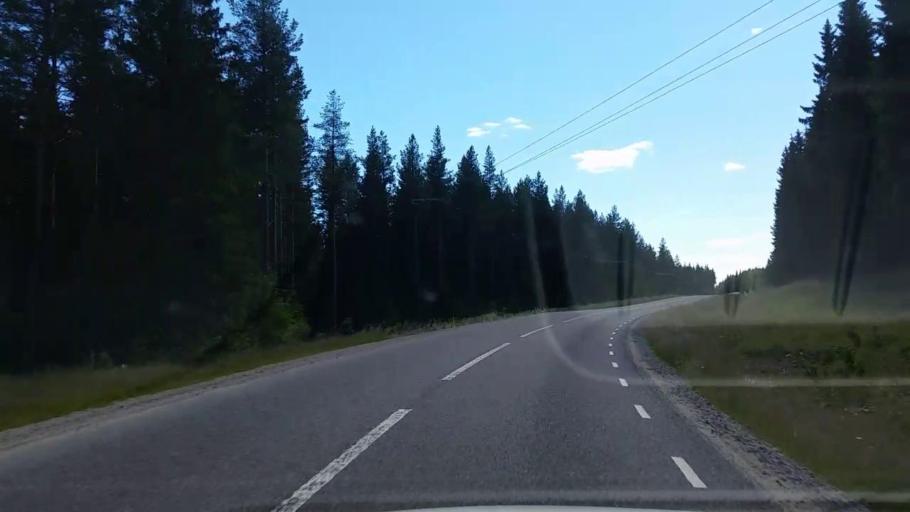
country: SE
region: Gaevleborg
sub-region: Ovanakers Kommun
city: Edsbyn
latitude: 61.5271
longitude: 15.6802
